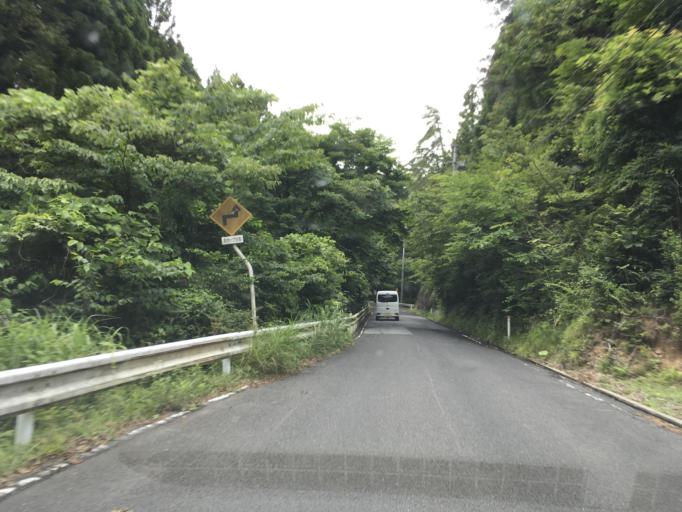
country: JP
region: Iwate
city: Ofunato
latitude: 38.9128
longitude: 141.6190
